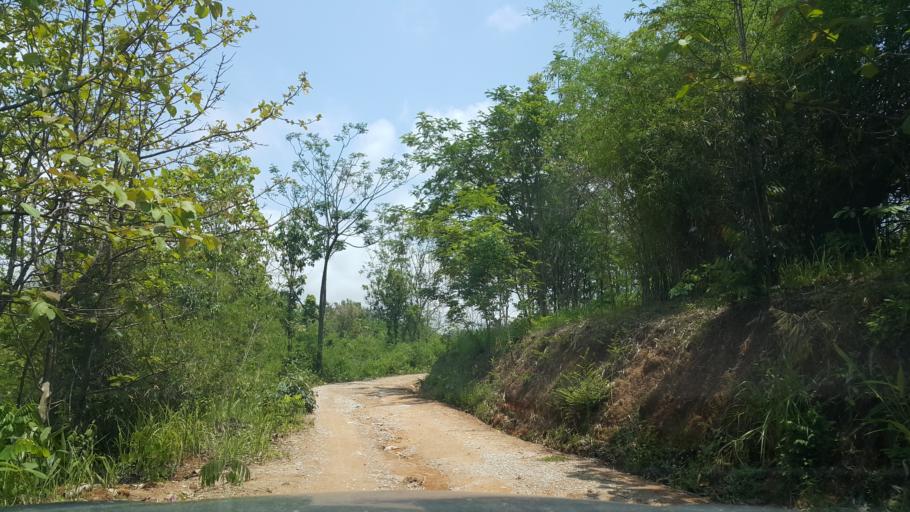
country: TH
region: Chiang Rai
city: Chiang Rai
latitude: 19.9988
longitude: 99.7181
